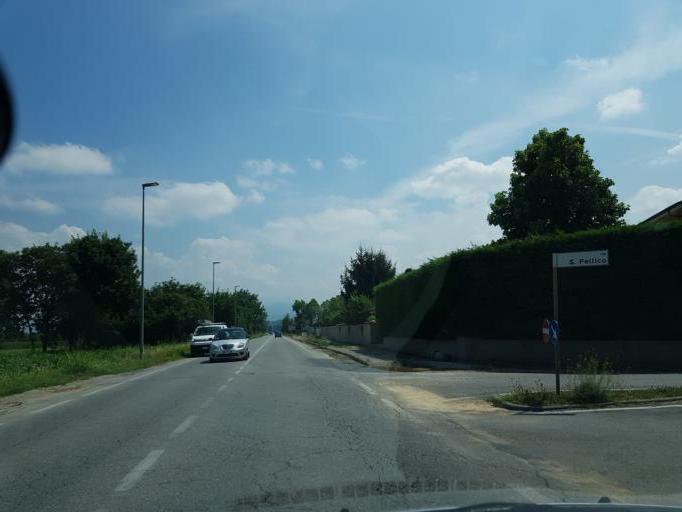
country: IT
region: Piedmont
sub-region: Provincia di Cuneo
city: Caraglio
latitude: 44.4122
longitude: 7.4388
